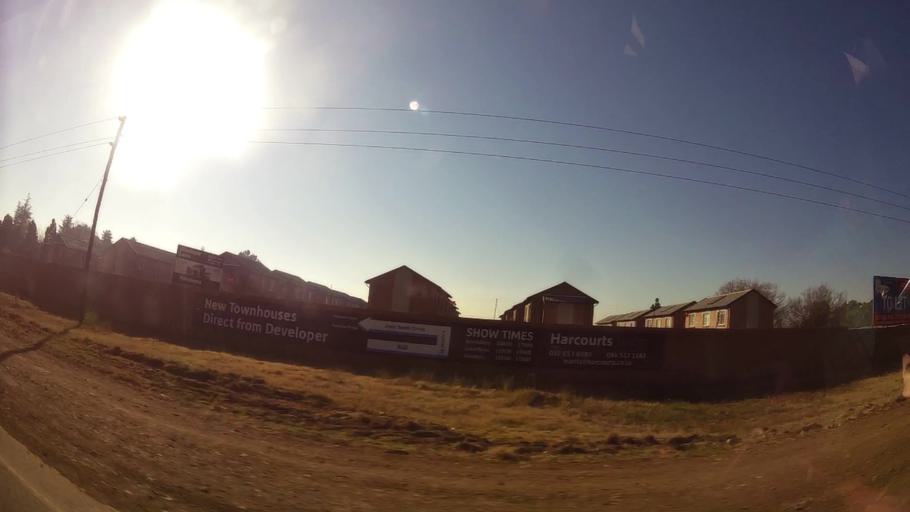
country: ZA
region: Gauteng
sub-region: City of Tshwane Metropolitan Municipality
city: Centurion
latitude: -25.8527
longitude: 28.1085
